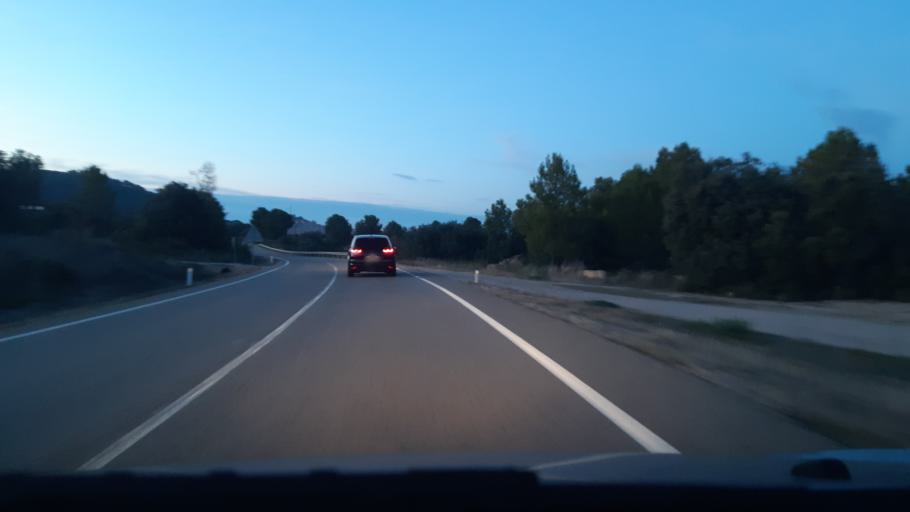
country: ES
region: Aragon
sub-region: Provincia de Teruel
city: Calaceite
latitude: 40.9985
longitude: 0.1957
